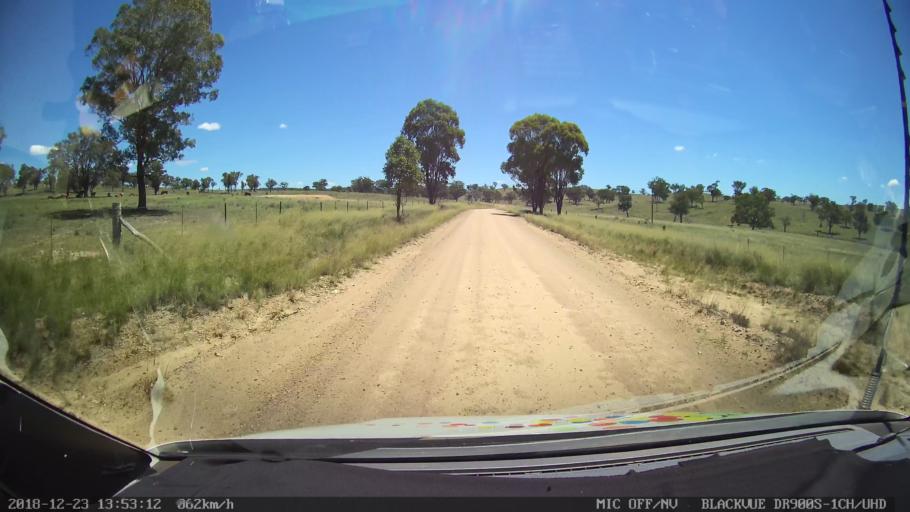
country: AU
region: New South Wales
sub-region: Tamworth Municipality
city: Manilla
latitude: -30.5517
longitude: 151.0968
